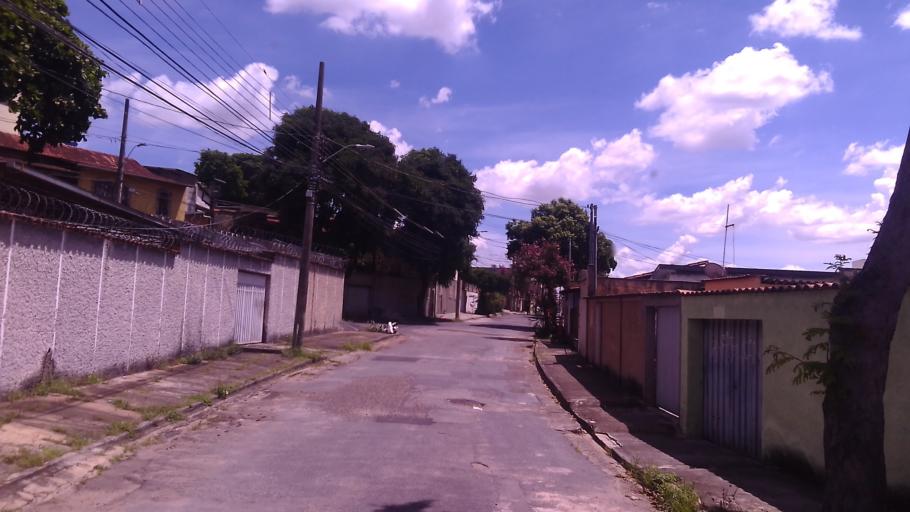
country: BR
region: Minas Gerais
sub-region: Contagem
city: Contagem
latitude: -19.9074
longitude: -44.0077
